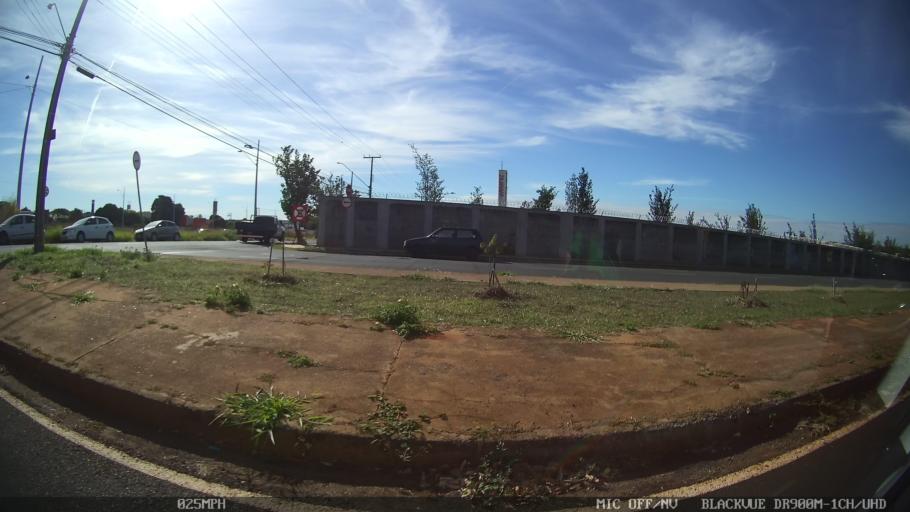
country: BR
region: Sao Paulo
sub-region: Sao Jose Do Rio Preto
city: Sao Jose do Rio Preto
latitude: -20.7897
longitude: -49.3535
